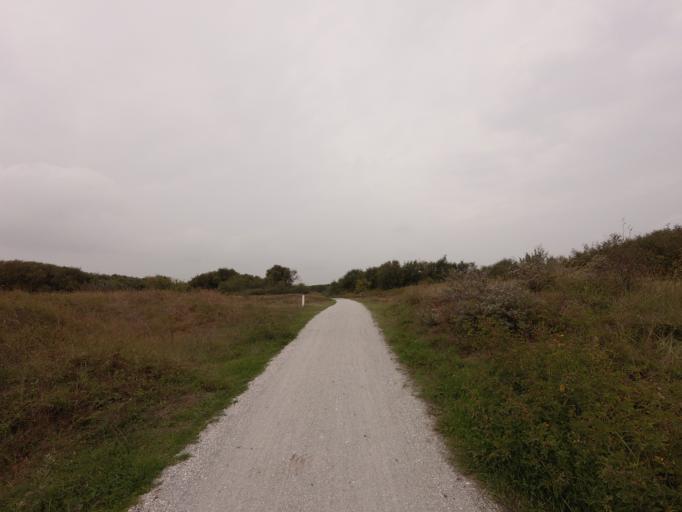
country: NL
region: Friesland
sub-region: Gemeente Schiermonnikoog
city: Schiermonnikoog
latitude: 53.4933
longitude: 6.1962
